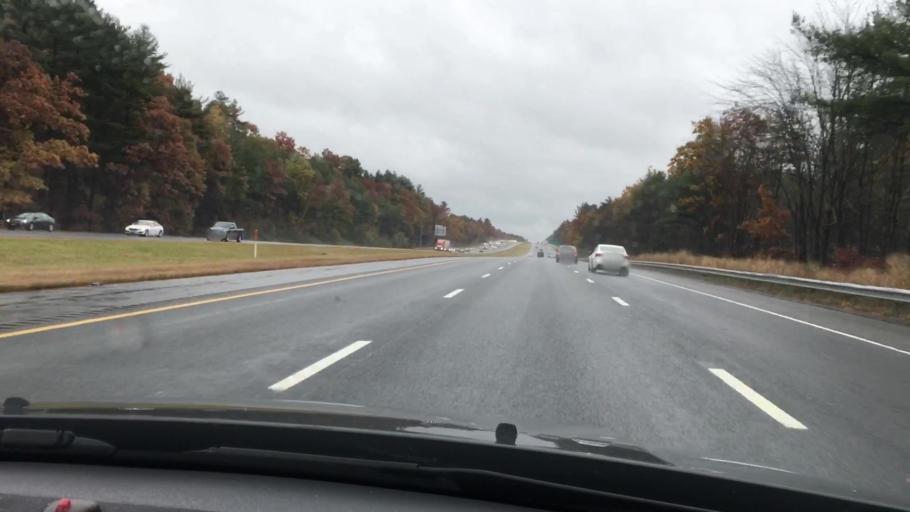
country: US
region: Massachusetts
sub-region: Middlesex County
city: Tyngsboro
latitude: 42.6664
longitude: -71.4349
